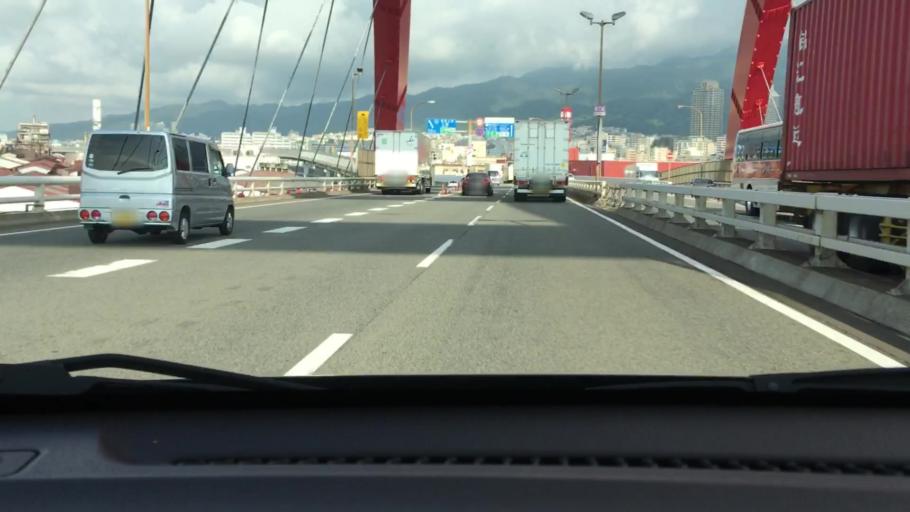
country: JP
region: Hyogo
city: Ashiya
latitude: 34.7075
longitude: 135.2511
